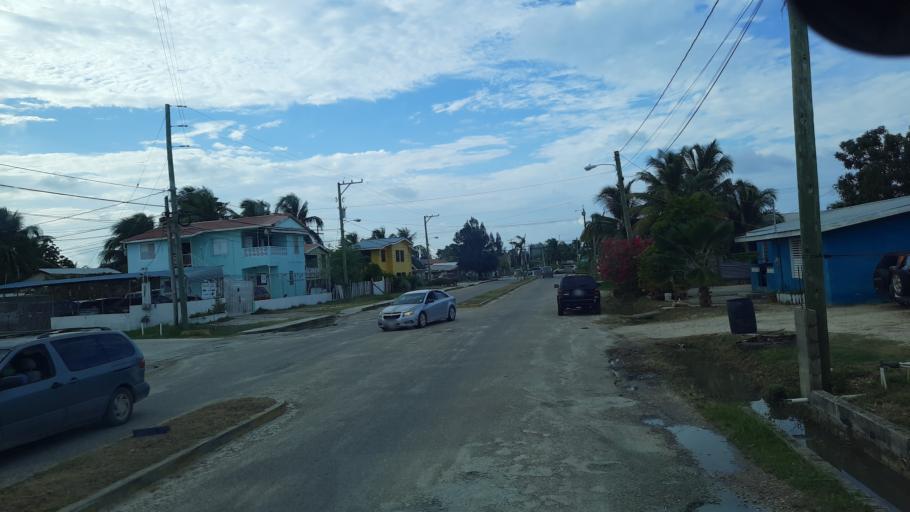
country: BZ
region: Belize
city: Belize City
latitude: 17.5006
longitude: -88.2061
